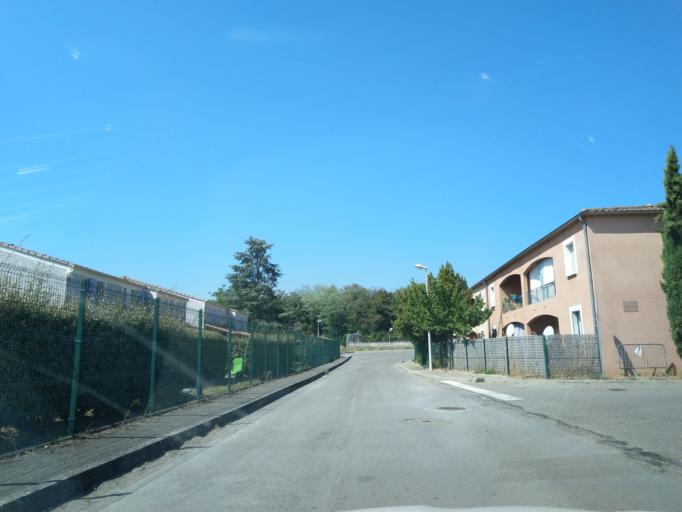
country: FR
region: Rhone-Alpes
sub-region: Departement de l'Ardeche
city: Ruoms
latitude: 44.4106
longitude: 4.4016
